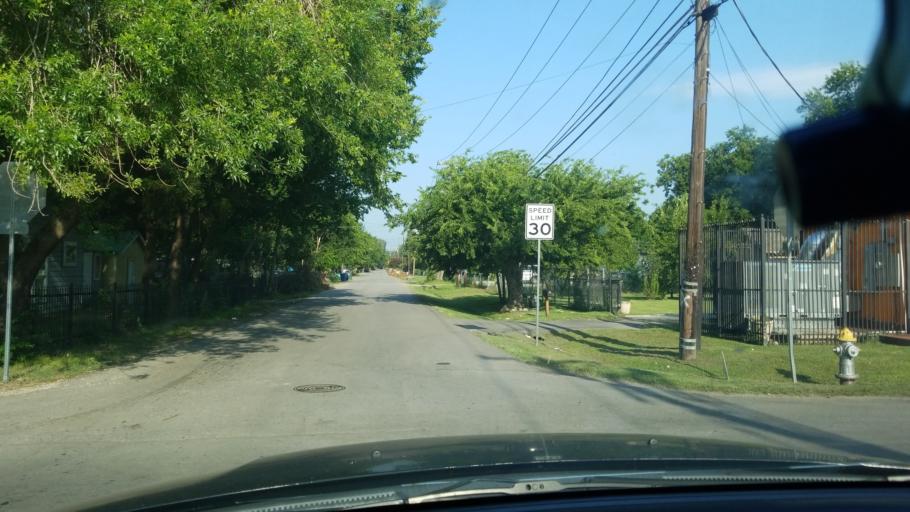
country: US
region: Texas
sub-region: Dallas County
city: Balch Springs
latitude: 32.7252
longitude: -96.6884
